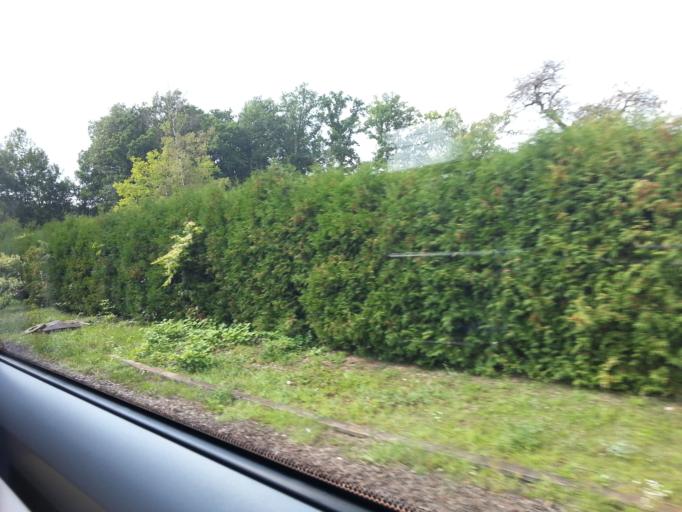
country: DE
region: Bavaria
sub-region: Regierungsbezirk Mittelfranken
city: Pleinfeld
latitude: 49.1040
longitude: 10.9726
